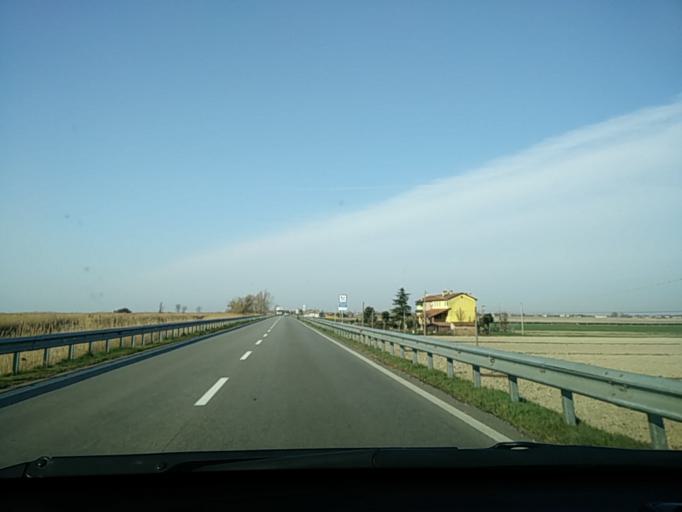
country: IT
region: Veneto
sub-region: Provincia di Venezia
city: Musile di Piave
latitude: 45.5760
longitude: 12.5354
